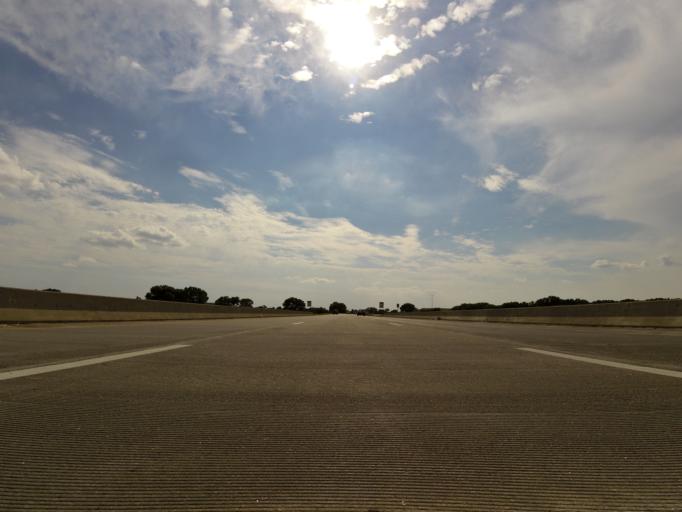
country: US
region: Kansas
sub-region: Sedgwick County
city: Wichita
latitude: 37.7554
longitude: -97.3808
